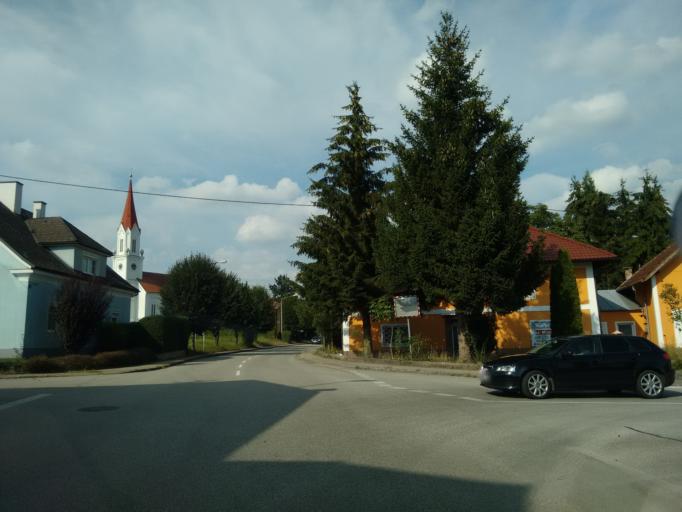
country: AT
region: Upper Austria
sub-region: Politischer Bezirk Grieskirchen
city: Bad Schallerbach
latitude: 48.2319
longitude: 13.9437
